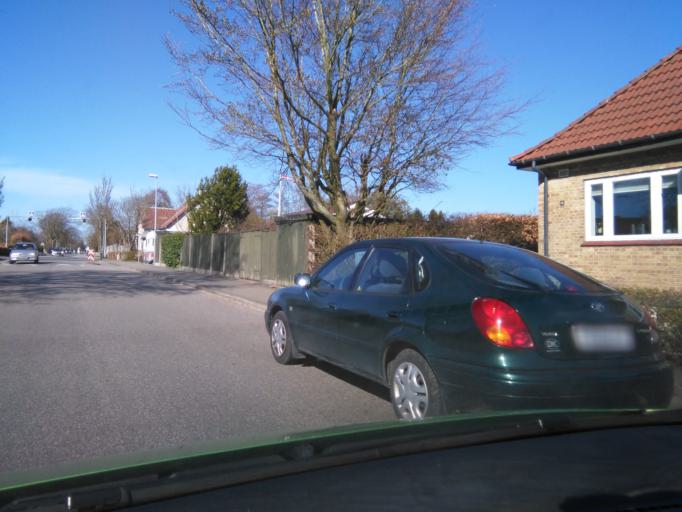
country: DK
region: South Denmark
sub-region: Varde Kommune
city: Oksbol
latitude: 55.6280
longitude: 8.2785
